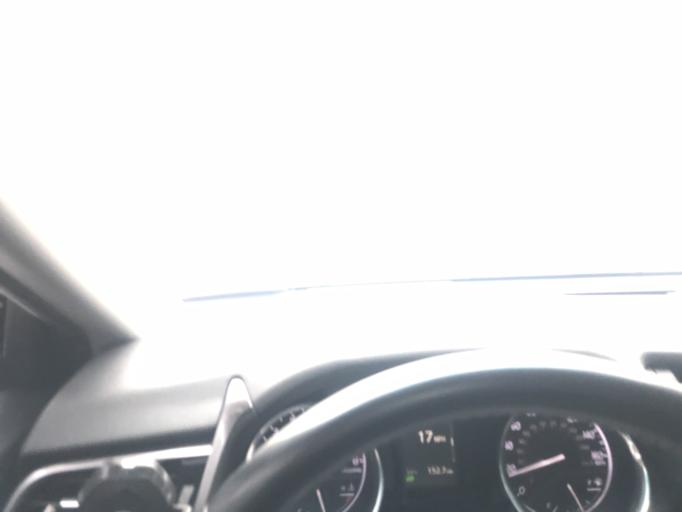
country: US
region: Massachusetts
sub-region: Norfolk County
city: Quincy
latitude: 42.2746
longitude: -71.0112
